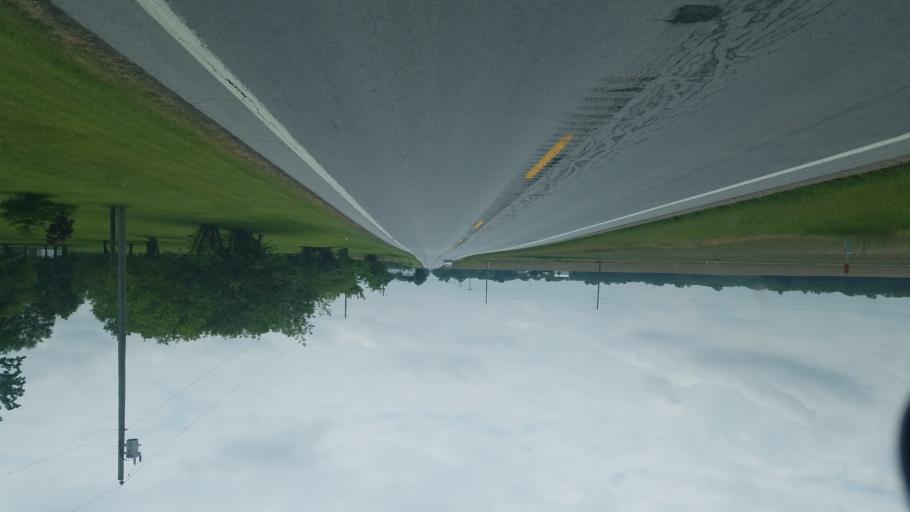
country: US
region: Ohio
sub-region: Union County
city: Richwood
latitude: 40.3575
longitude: -83.2972
